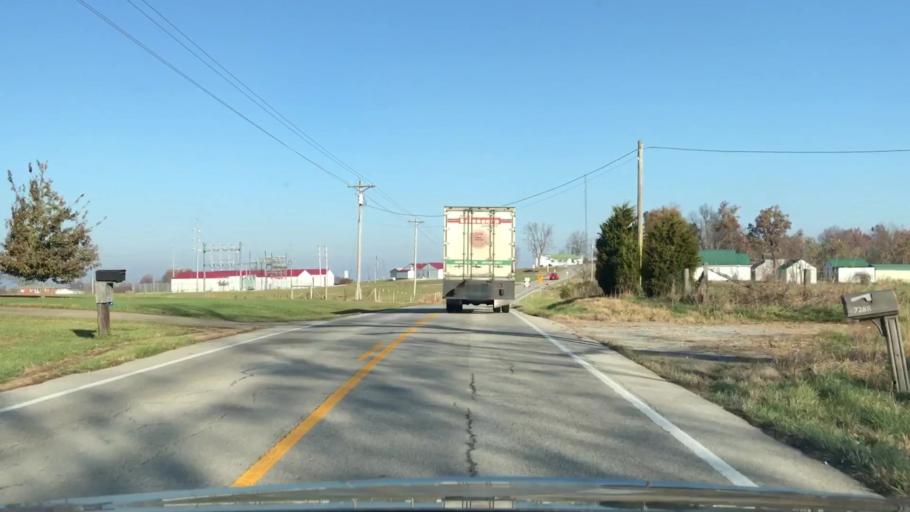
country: US
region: Kentucky
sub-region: Grayson County
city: Leitchfield
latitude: 37.4009
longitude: -86.2374
